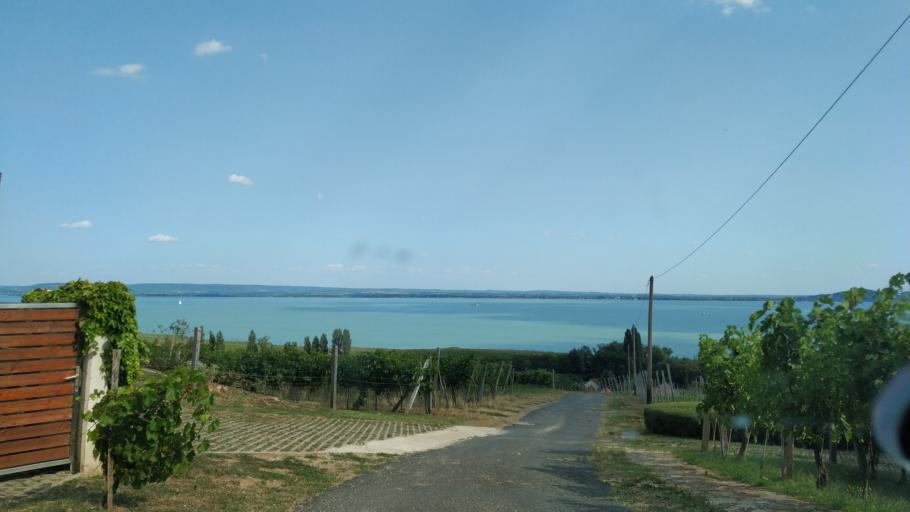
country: HU
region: Veszprem
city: Badacsonytomaj
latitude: 46.8088
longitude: 17.5417
